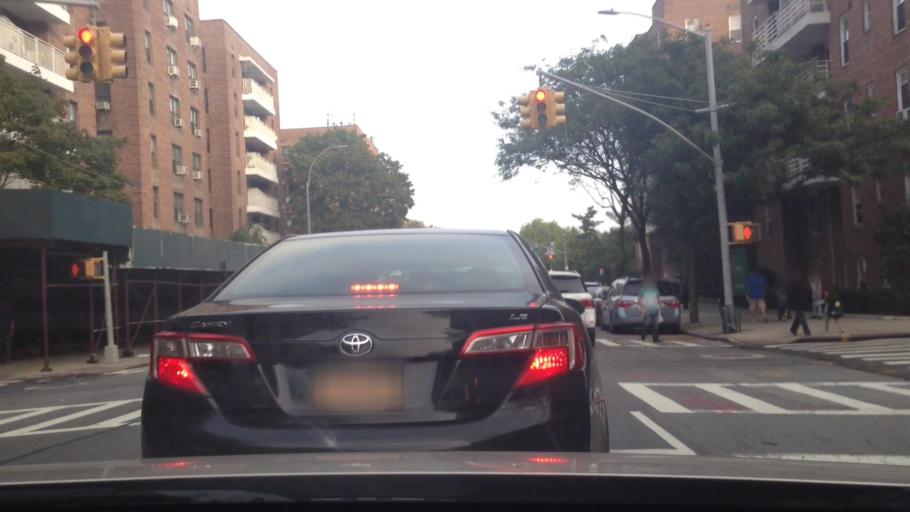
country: US
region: New York
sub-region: Queens County
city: Borough of Queens
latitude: 40.7348
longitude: -73.8506
